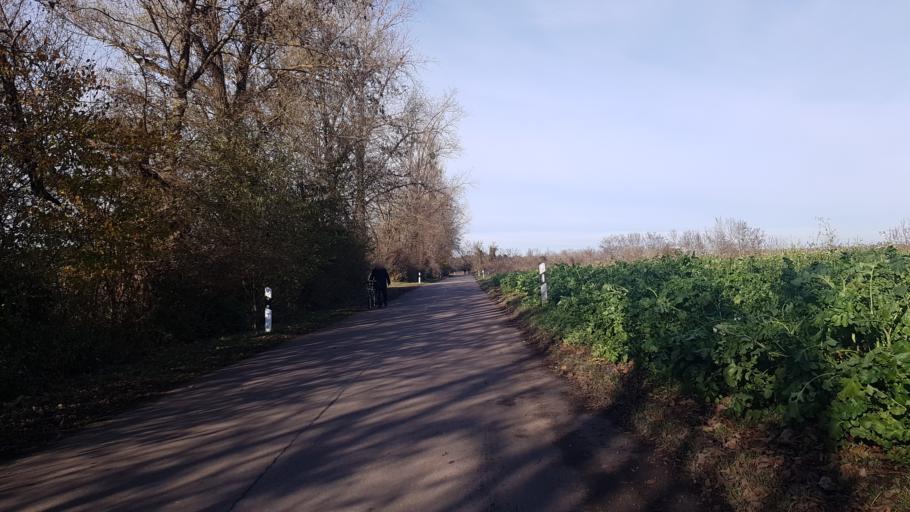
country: DE
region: Bavaria
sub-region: Upper Bavaria
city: Karlsfeld
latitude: 48.2334
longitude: 11.5049
